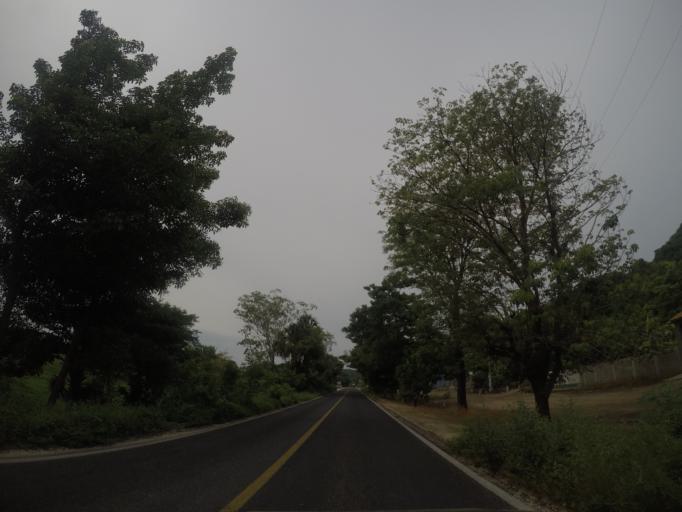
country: MX
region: Oaxaca
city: San Pedro Mixtepec
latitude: 15.9569
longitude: -97.2523
